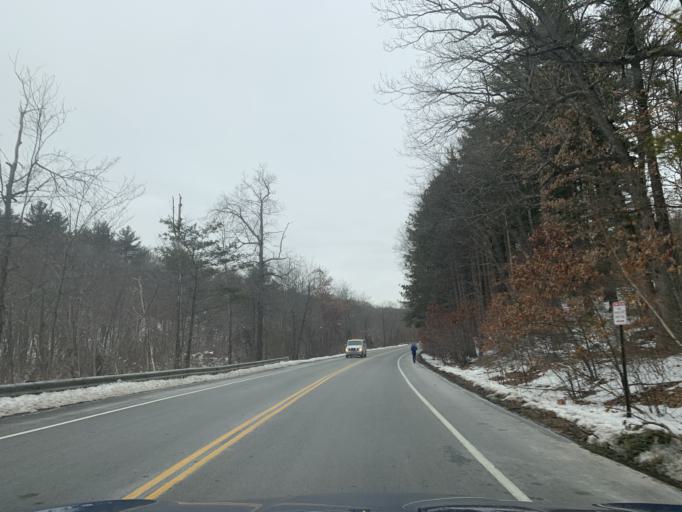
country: US
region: Massachusetts
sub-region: Norfolk County
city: Milton
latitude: 42.2371
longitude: -71.0919
